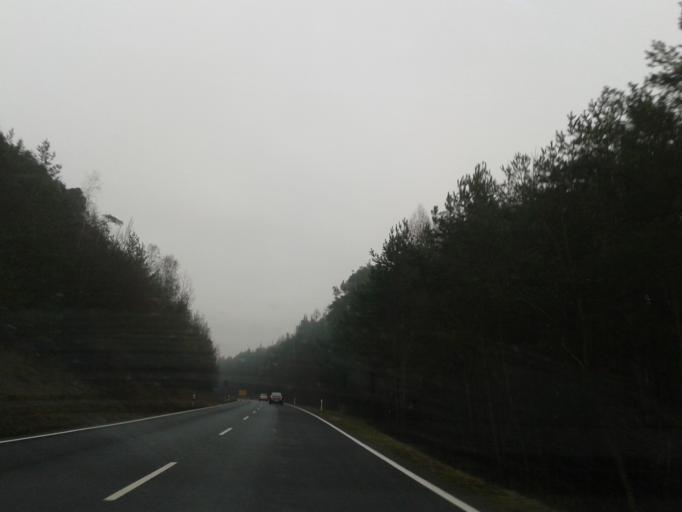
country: DE
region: Bavaria
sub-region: Regierungsbezirk Unterfranken
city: Burgpreppach
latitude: 50.1531
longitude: 10.6767
